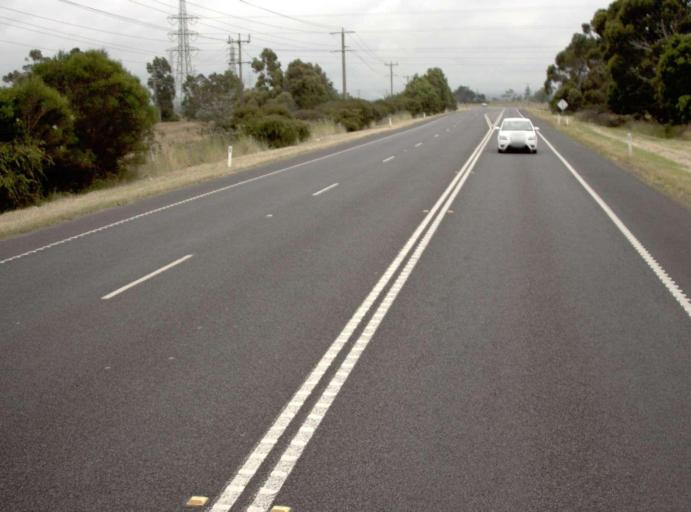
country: AU
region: Victoria
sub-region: Latrobe
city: Morwell
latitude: -38.2724
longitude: 146.4223
